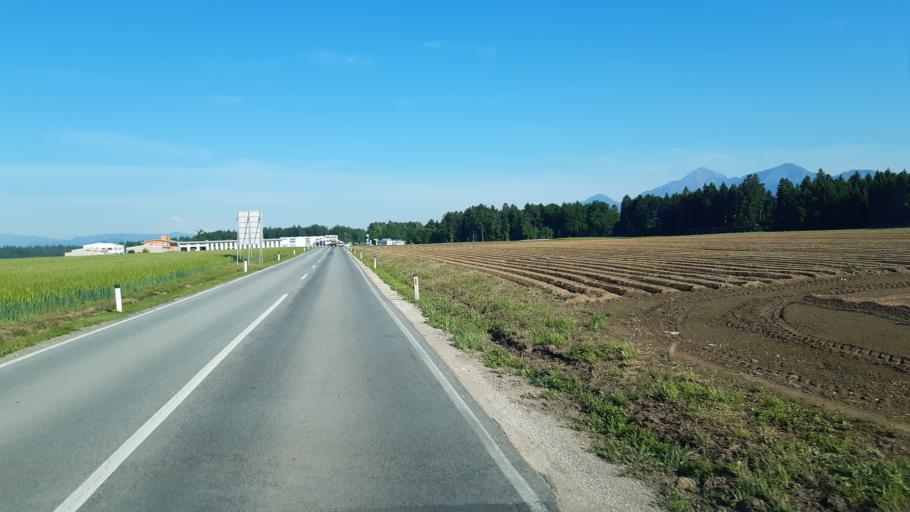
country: SI
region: Komenda
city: Komenda
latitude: 46.2024
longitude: 14.5309
